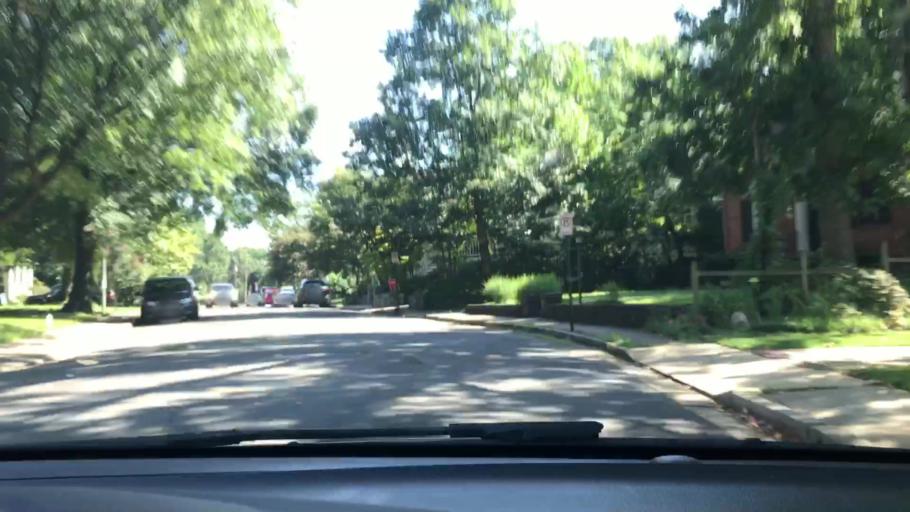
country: US
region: Virginia
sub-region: Arlington County
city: Arlington
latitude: 38.8809
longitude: -77.0988
